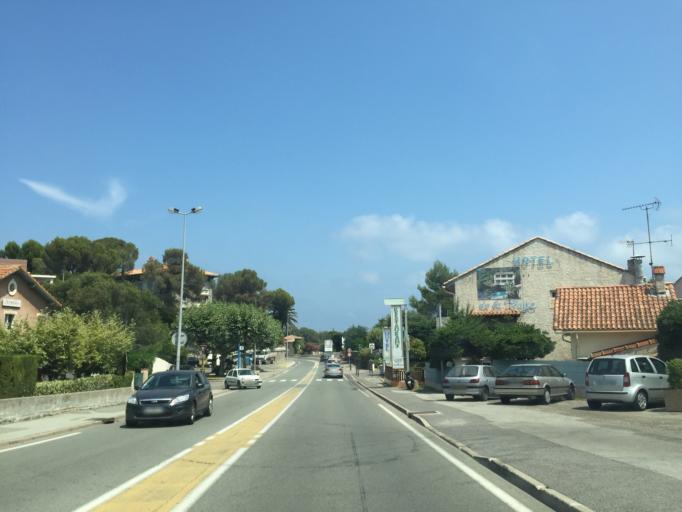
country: FR
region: Provence-Alpes-Cote d'Azur
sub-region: Departement du Var
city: Saint-Raphael
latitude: 43.4200
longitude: 6.8547
